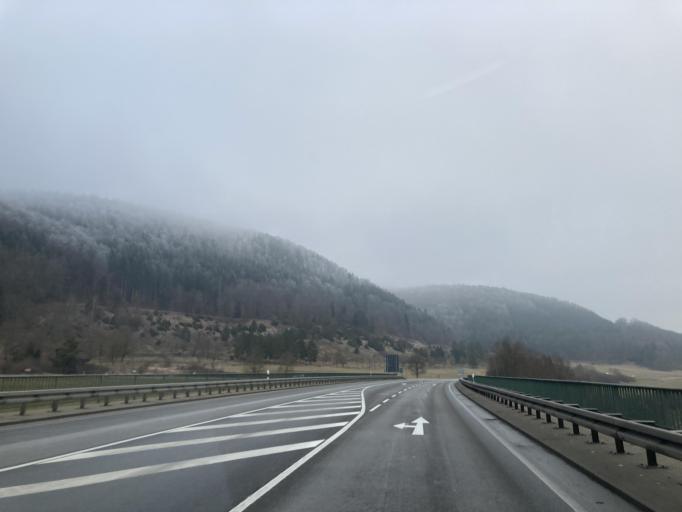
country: DE
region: Baden-Wuerttemberg
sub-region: Freiburg Region
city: Geisingen
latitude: 47.9244
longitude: 8.6757
